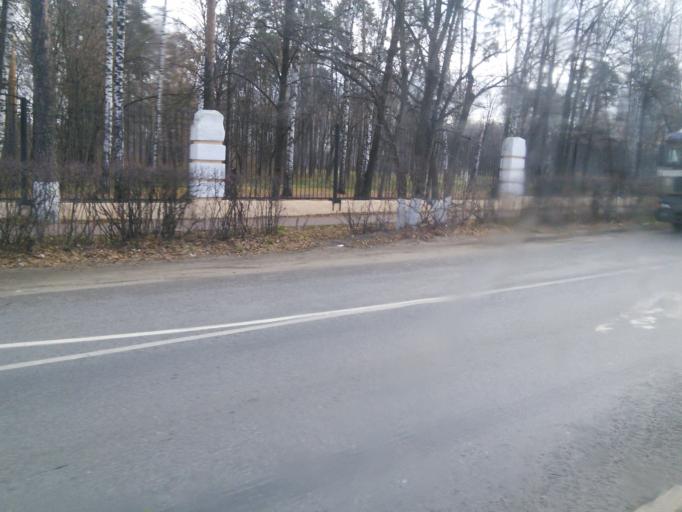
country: RU
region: Moskovskaya
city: Likino-Dulevo
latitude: 55.7079
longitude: 38.9578
